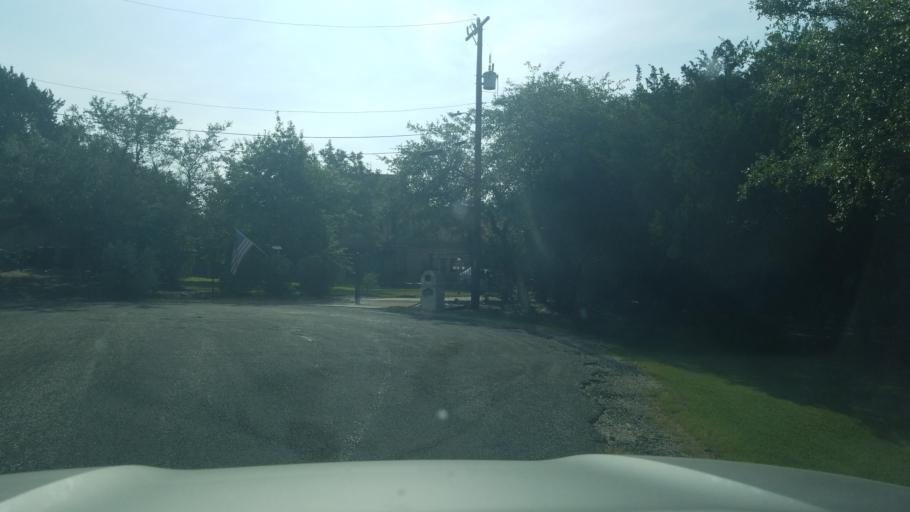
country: US
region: Texas
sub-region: Bexar County
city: Timberwood Park
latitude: 29.6975
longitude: -98.4931
